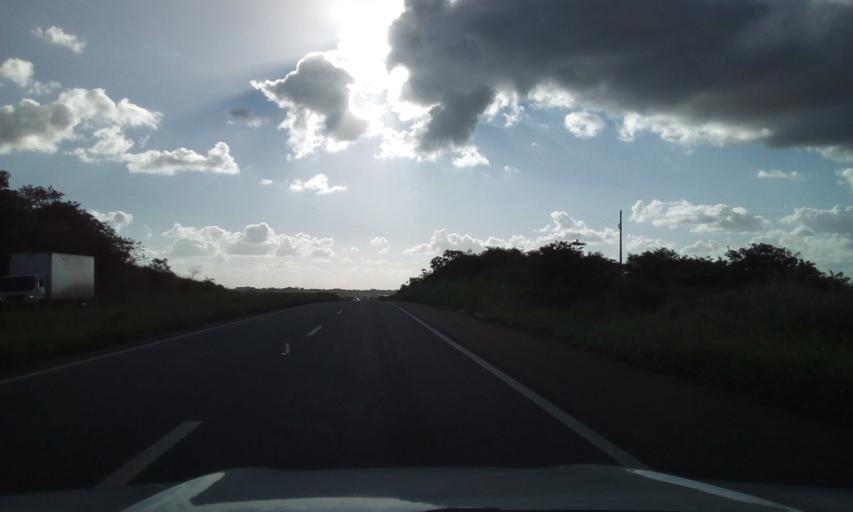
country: BR
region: Paraiba
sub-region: Cruz Do Espirito Santo
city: Cruz do Espirito Santo
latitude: -7.1965
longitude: -35.1705
